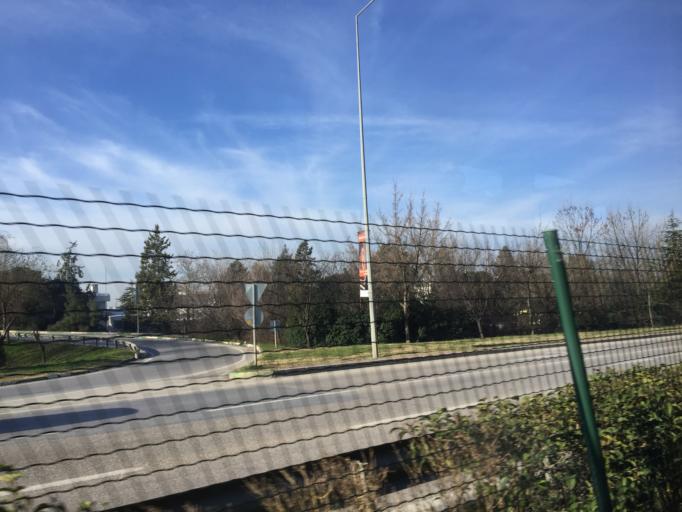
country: TR
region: Bursa
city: Niluefer
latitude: 40.2394
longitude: 28.9722
